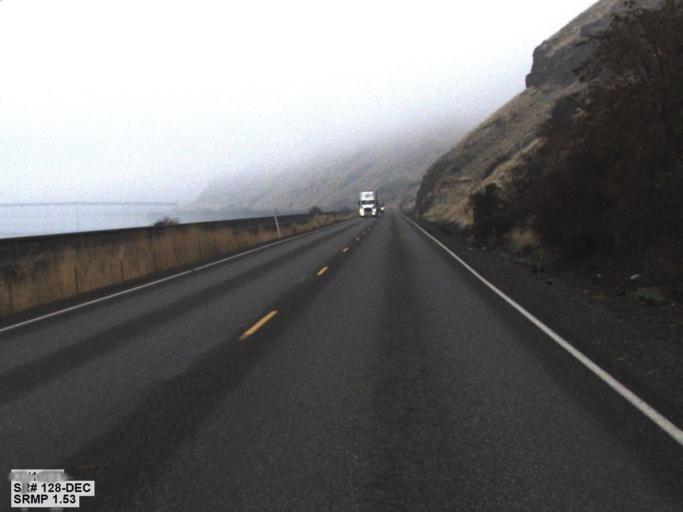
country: US
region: Washington
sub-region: Asotin County
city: Clarkston
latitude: 46.4318
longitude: -117.0544
